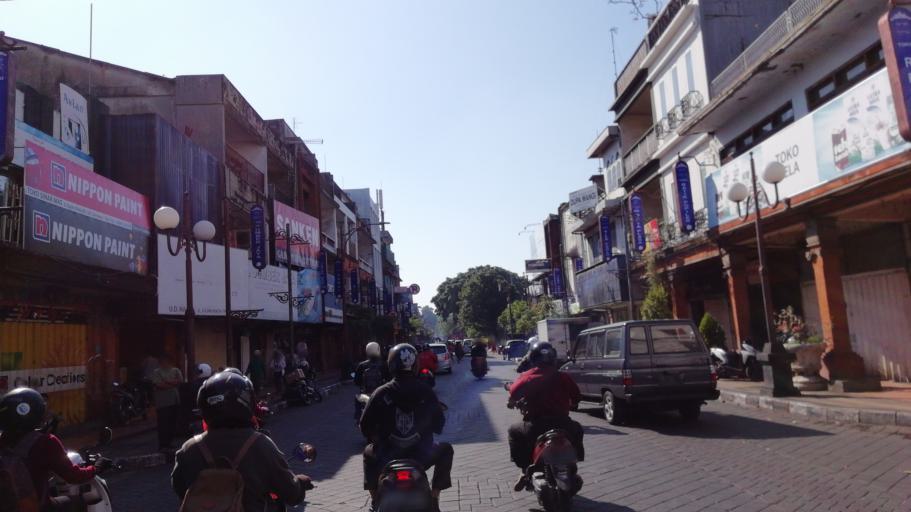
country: ID
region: Bali
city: Denpasar
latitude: -8.6552
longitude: 115.2113
